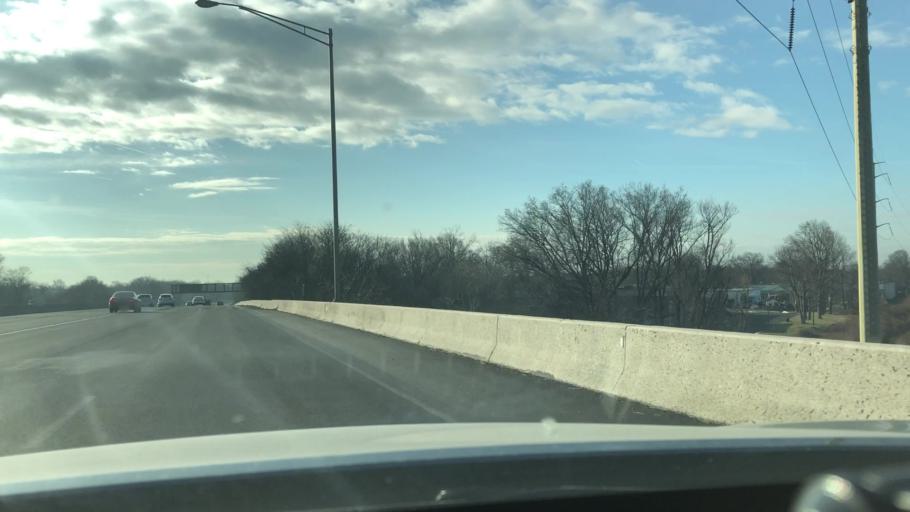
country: US
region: New Jersey
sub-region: Union County
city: Winfield
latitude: 40.6538
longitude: -74.2874
